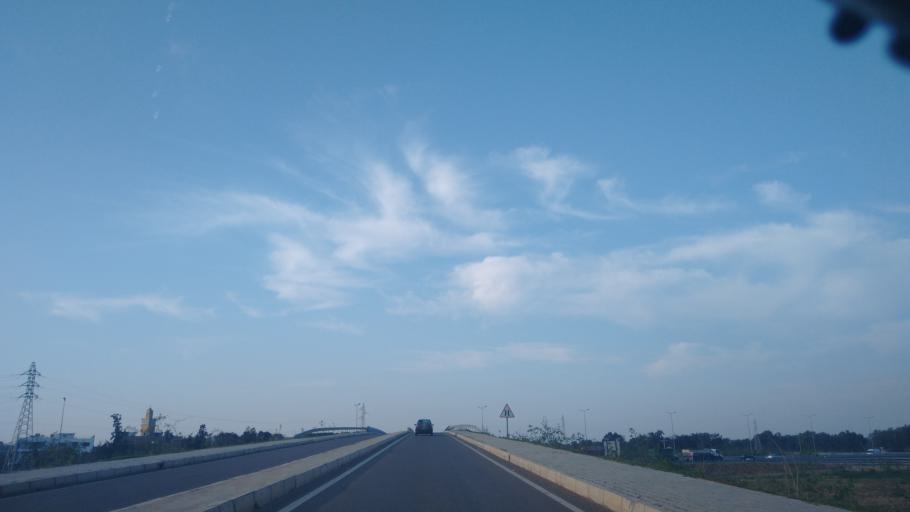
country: MA
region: Rabat-Sale-Zemmour-Zaer
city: Sale
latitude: 33.9990
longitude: -6.7186
